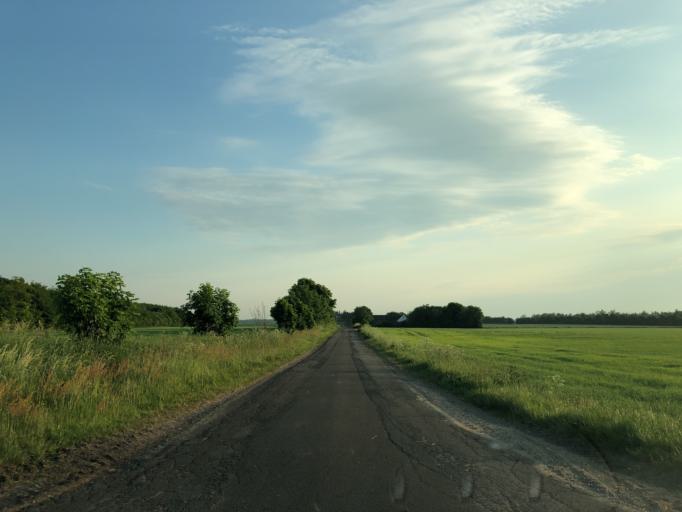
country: DK
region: Central Jutland
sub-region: Holstebro Kommune
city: Holstebro
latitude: 56.3940
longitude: 8.4812
